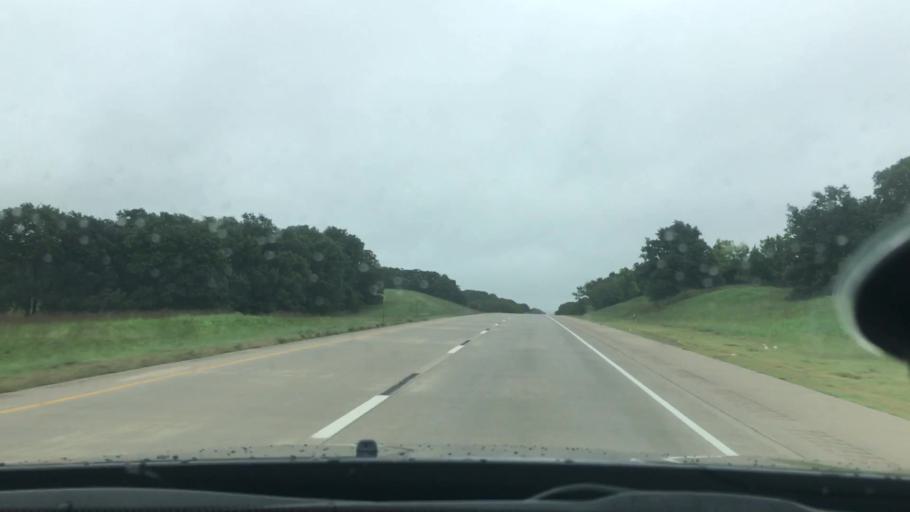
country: US
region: Oklahoma
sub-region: Lincoln County
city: Prague
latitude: 35.3846
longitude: -96.5839
